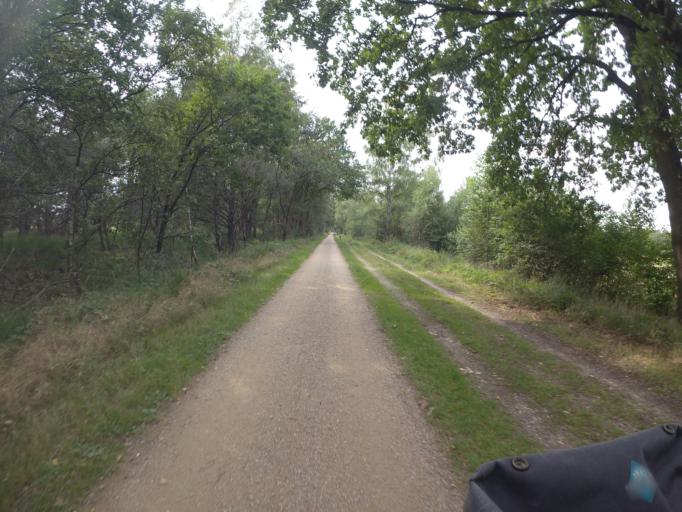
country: NL
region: Limburg
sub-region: Gemeente Bergen
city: Wellerlooi
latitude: 51.5899
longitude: 6.0979
